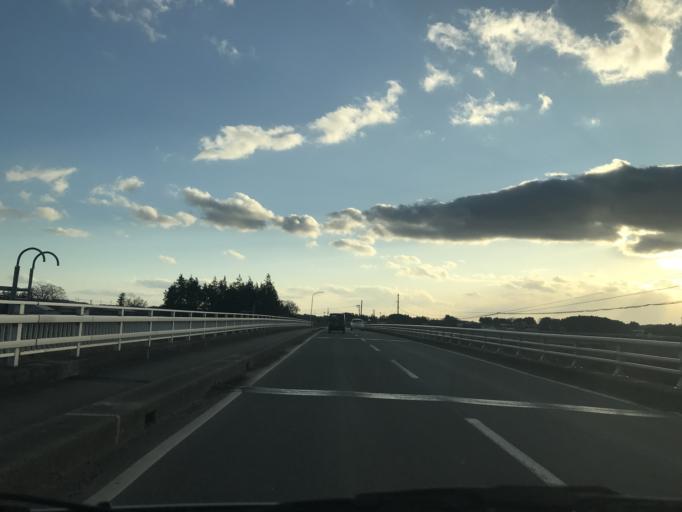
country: JP
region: Miyagi
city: Kogota
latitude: 38.6454
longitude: 141.0745
